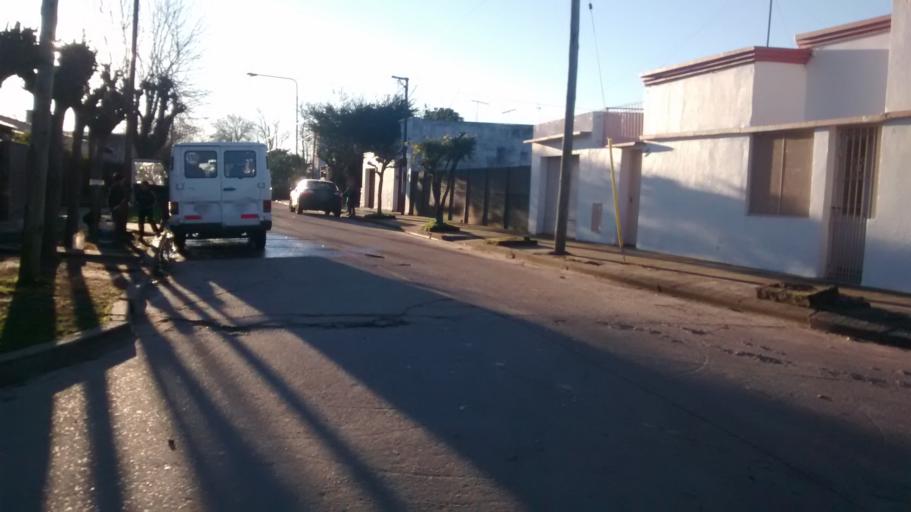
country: AR
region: Buenos Aires
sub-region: Partido de La Plata
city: La Plata
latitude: -34.9605
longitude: -57.9453
